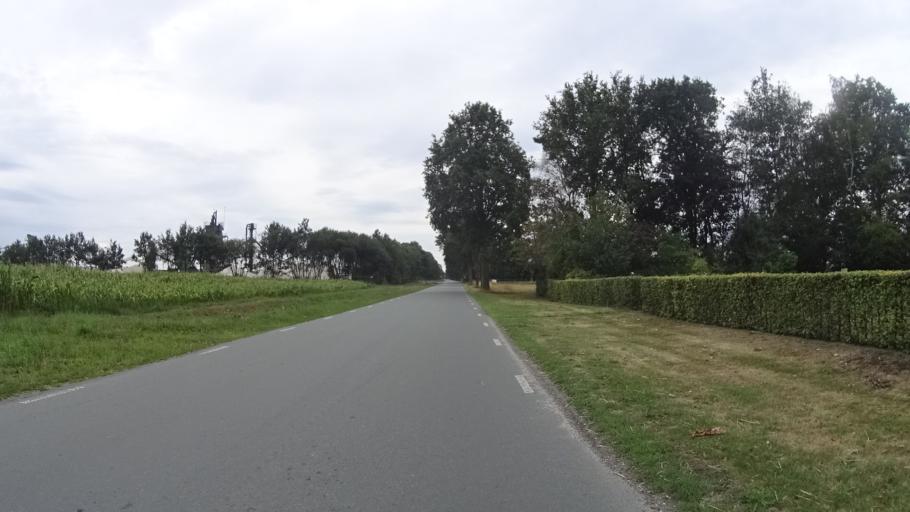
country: NL
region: Groningen
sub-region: Gemeente Slochteren
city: Slochteren
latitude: 53.1871
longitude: 6.8506
